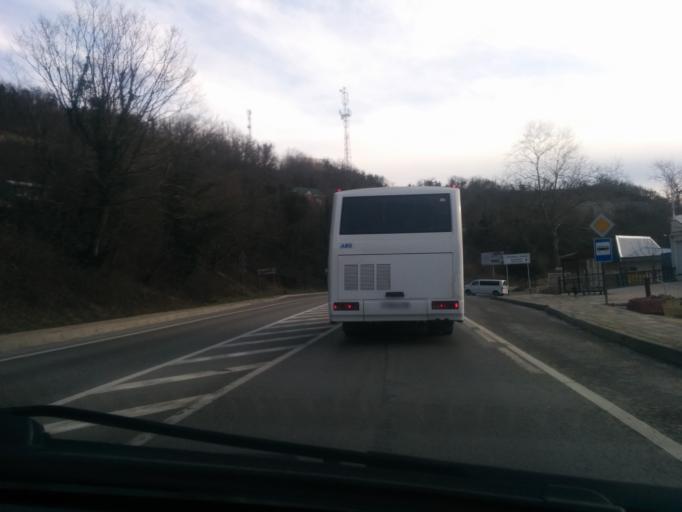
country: RU
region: Krasnodarskiy
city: Ol'ginka
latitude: 44.1957
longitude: 38.8917
